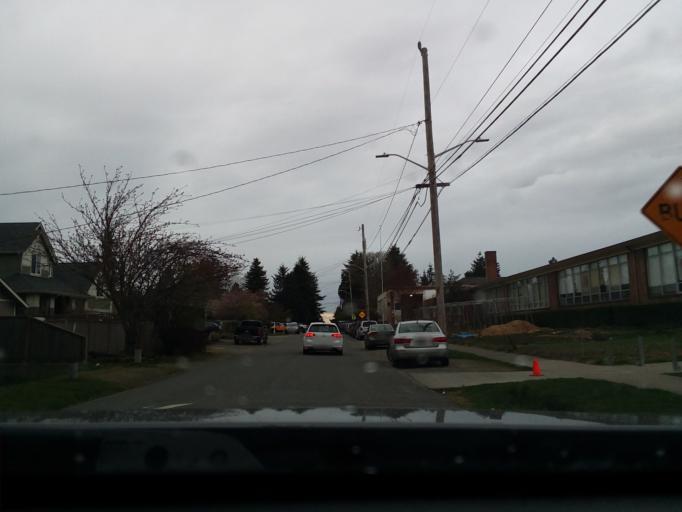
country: US
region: Washington
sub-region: King County
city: Shoreline
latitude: 47.6965
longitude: -122.3741
